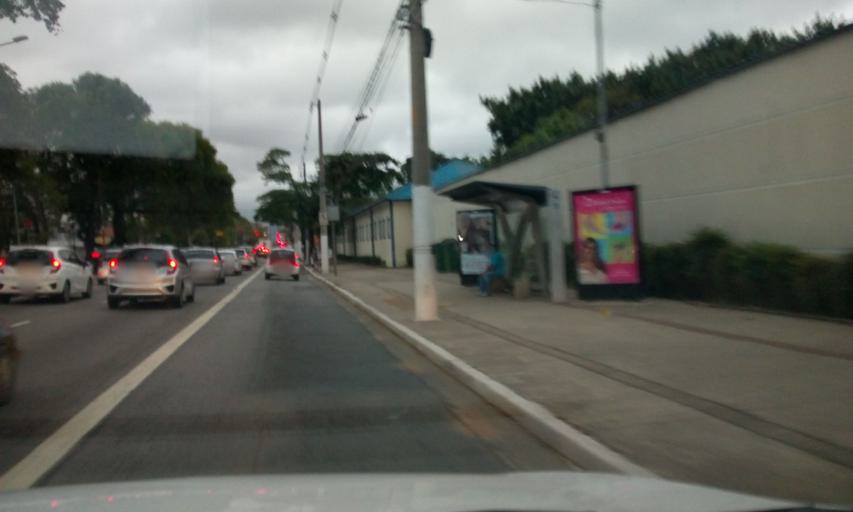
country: BR
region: Sao Paulo
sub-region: Sao Paulo
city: Sao Paulo
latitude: -23.5279
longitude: -46.6253
